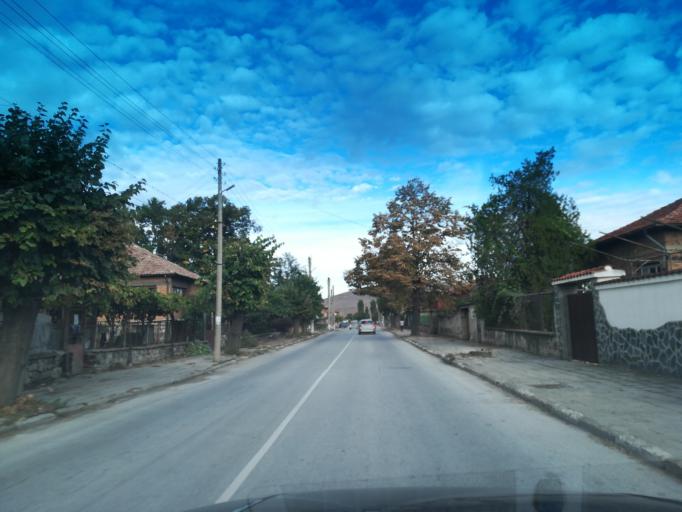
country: BG
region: Plovdiv
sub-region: Obshtina Krichim
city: Krichim
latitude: 42.0854
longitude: 24.4322
